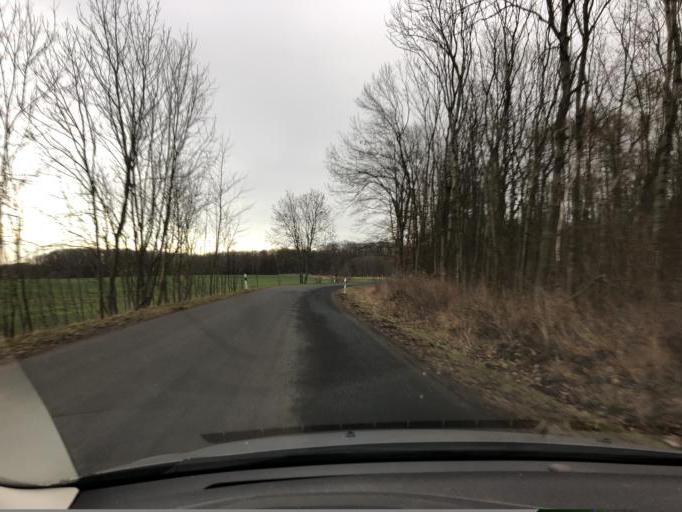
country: DE
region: Thuringia
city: Ramsla
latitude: 51.0333
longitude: 11.2599
